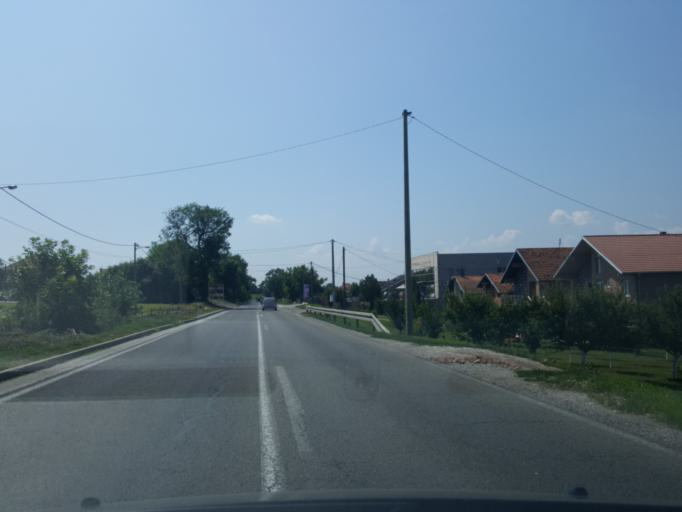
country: RS
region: Central Serbia
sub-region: Belgrade
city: Mladenovac
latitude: 44.4672
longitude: 20.6670
